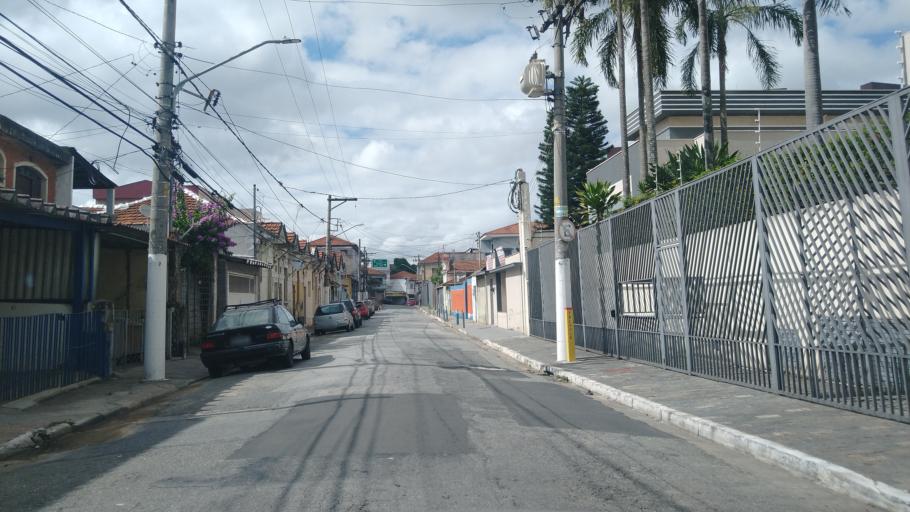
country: BR
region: Sao Paulo
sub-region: Sao Paulo
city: Sao Paulo
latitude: -23.4989
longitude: -46.6106
